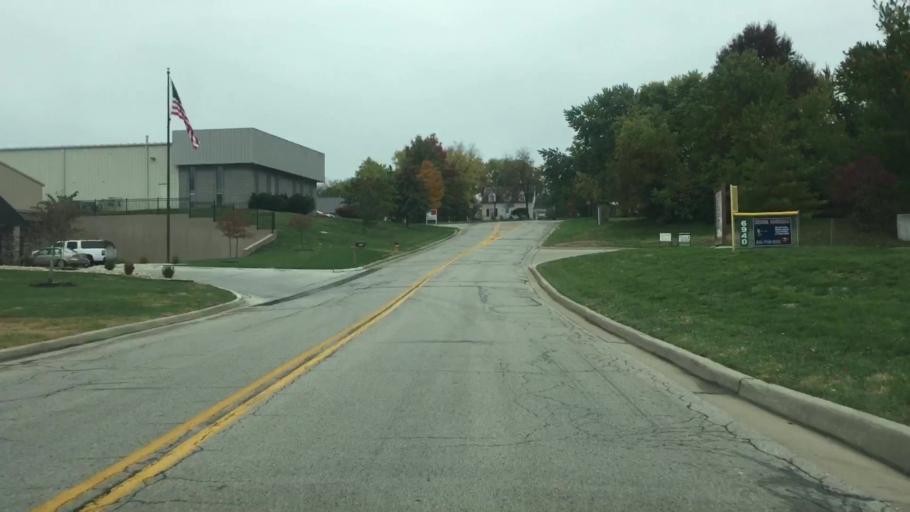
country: US
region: Kansas
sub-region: Wyandotte County
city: Edwardsville
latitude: 39.0014
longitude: -94.8245
